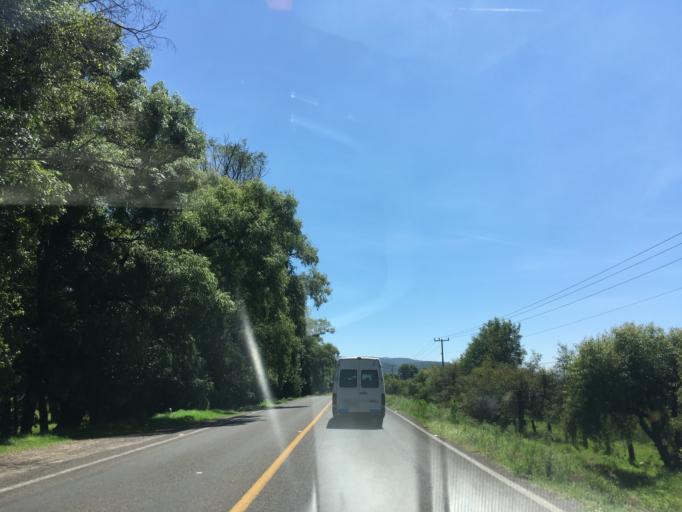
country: MX
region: Michoacan
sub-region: Hidalgo
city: San Lucas Huarirapeo (La Mesa de San Lucas)
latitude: 19.6894
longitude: -100.6250
